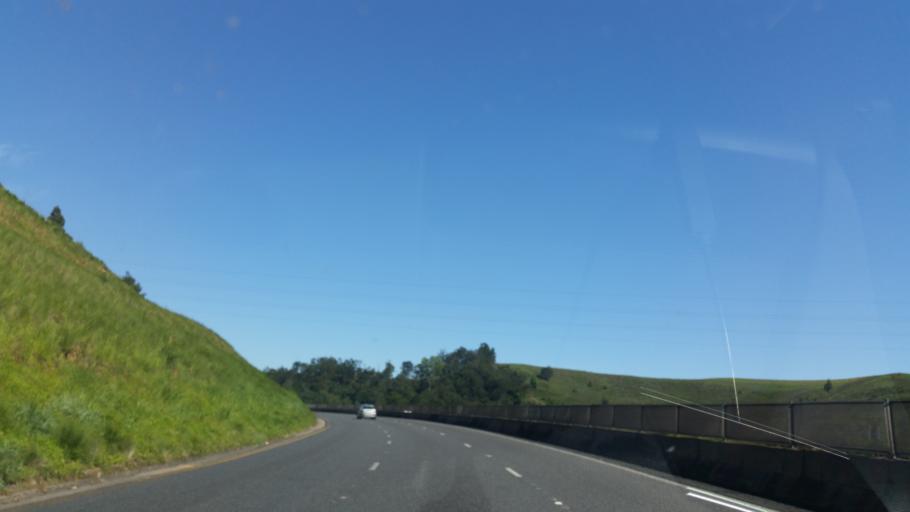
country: ZA
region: KwaZulu-Natal
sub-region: uMgungundlovu District Municipality
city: Mooirivier
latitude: -29.3340
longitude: 30.0683
